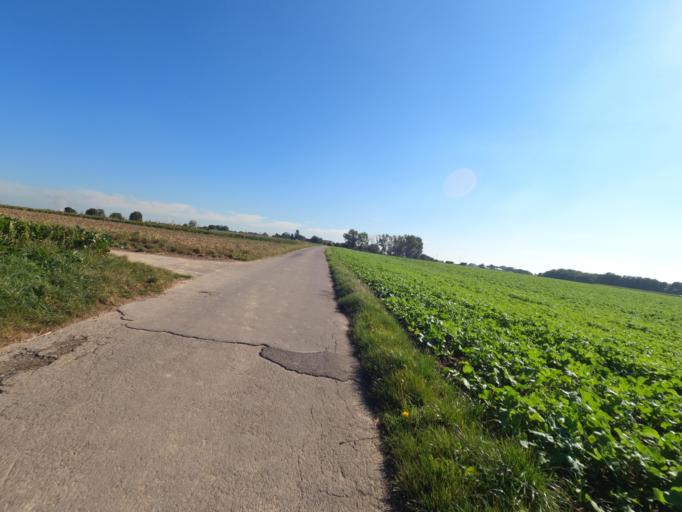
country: DE
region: North Rhine-Westphalia
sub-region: Regierungsbezirk Koln
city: Linnich
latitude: 50.9907
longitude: 6.2996
